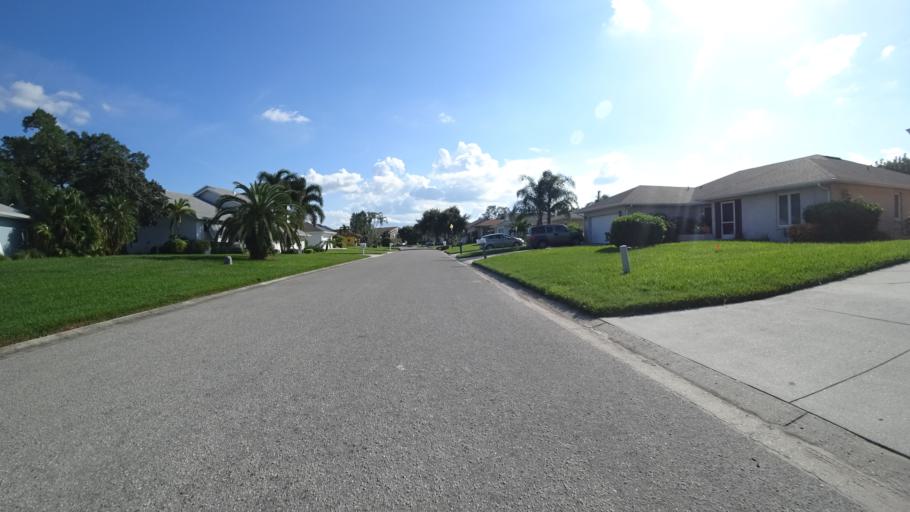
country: US
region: Florida
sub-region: Manatee County
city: Cortez
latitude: 27.4529
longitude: -82.6511
